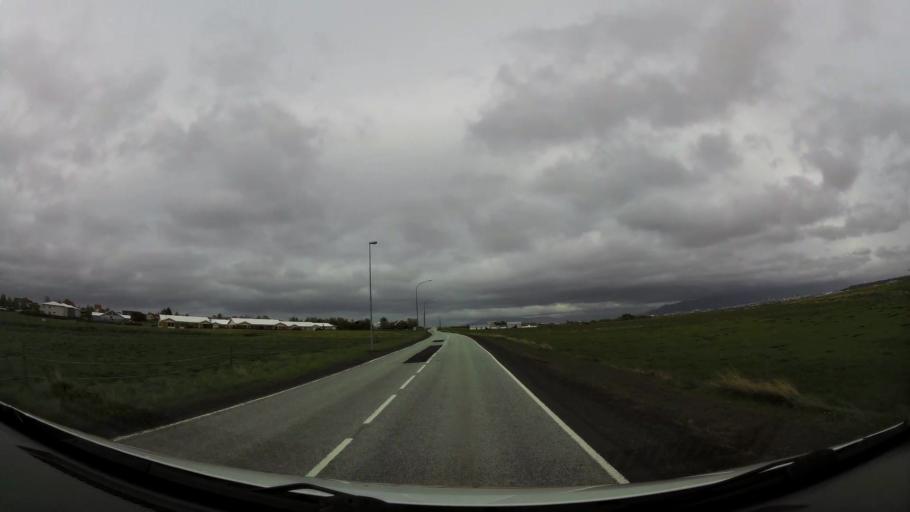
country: IS
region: Capital Region
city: Alftanes
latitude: 64.1033
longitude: -22.0097
